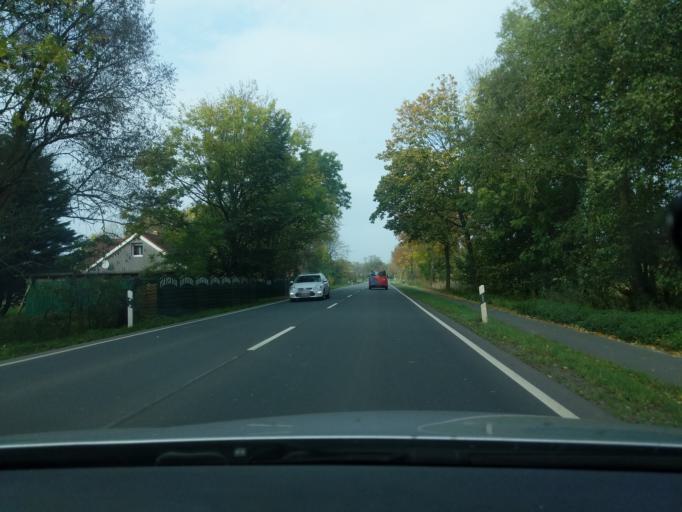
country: DE
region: Lower Saxony
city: Belum
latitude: 53.8114
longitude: 8.9966
